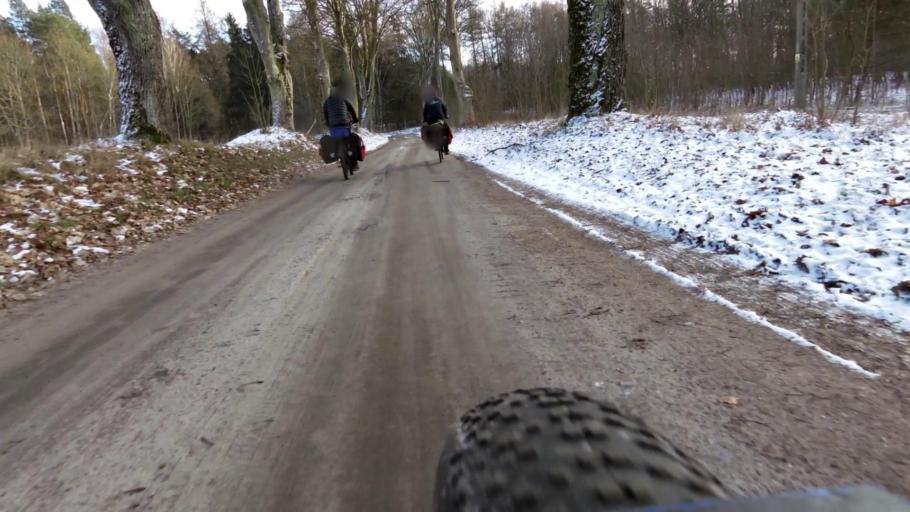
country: PL
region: West Pomeranian Voivodeship
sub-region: Powiat walecki
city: Walcz
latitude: 53.2635
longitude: 16.3144
